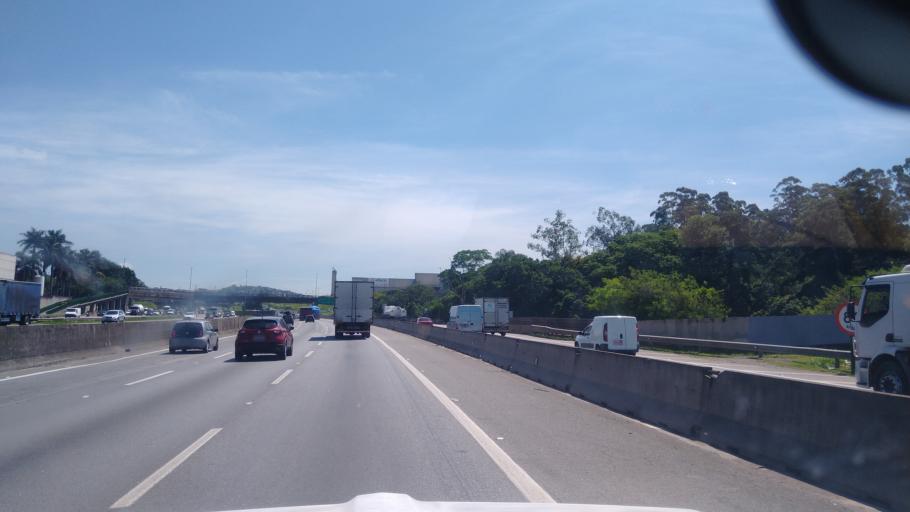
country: BR
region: Sao Paulo
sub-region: Itaquaquecetuba
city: Itaquaquecetuba
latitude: -23.4776
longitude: -46.4380
